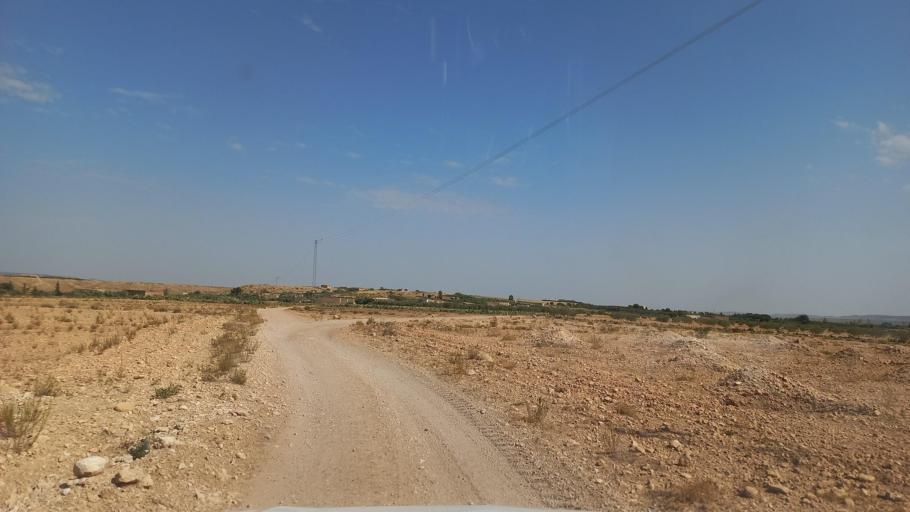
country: TN
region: Al Qasrayn
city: Kasserine
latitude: 35.2791
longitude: 8.9631
